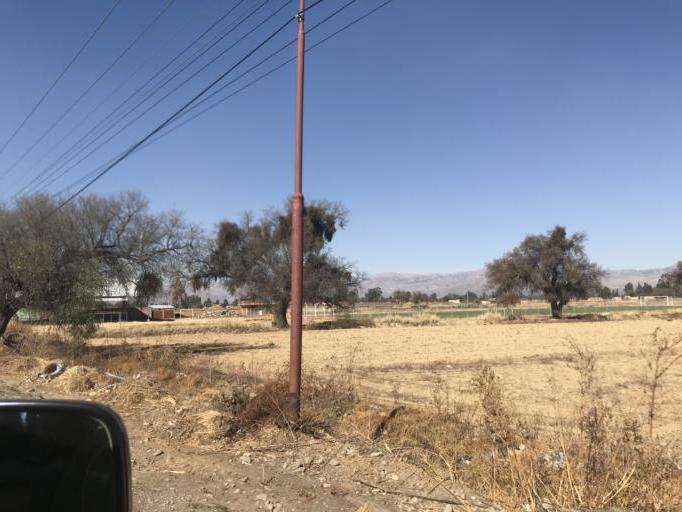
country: BO
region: Cochabamba
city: Punata
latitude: -17.5601
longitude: -65.8715
